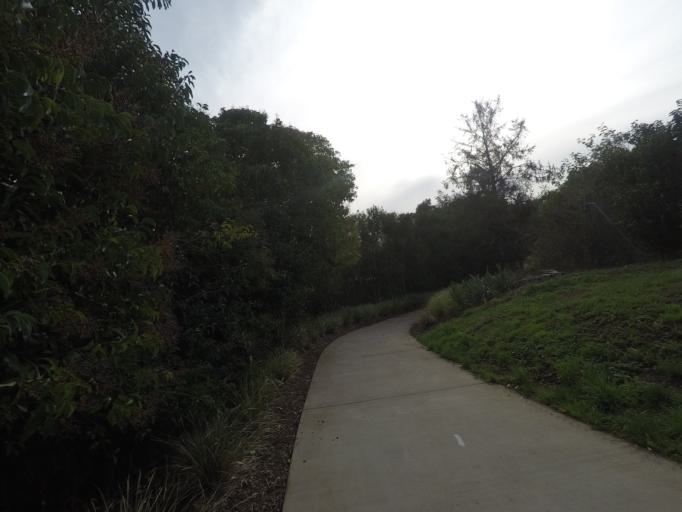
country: NZ
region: Auckland
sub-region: Auckland
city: Mangere
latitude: -36.9472
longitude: 174.8054
